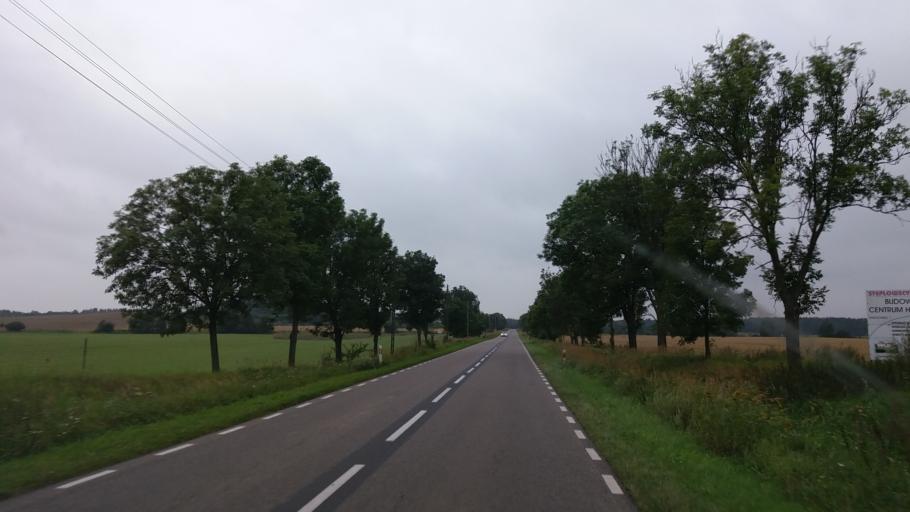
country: PL
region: West Pomeranian Voivodeship
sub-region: Powiat choszczenski
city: Pelczyce
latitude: 53.0200
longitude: 15.2805
